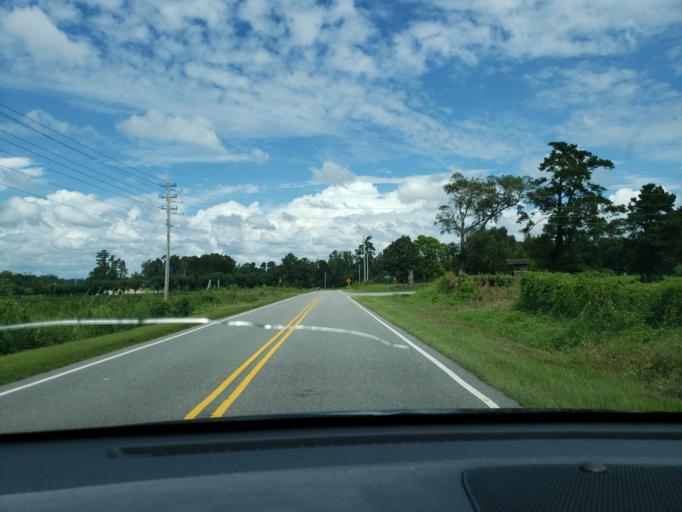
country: US
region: North Carolina
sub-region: Columbus County
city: Tabor City
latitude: 34.1736
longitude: -78.7850
